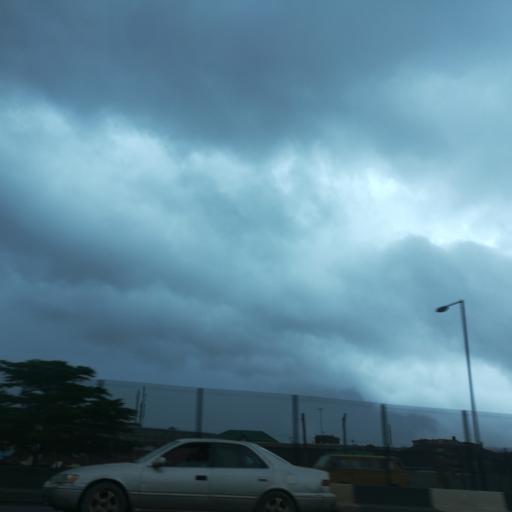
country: NG
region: Lagos
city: Somolu
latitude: 6.5530
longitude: 3.3970
